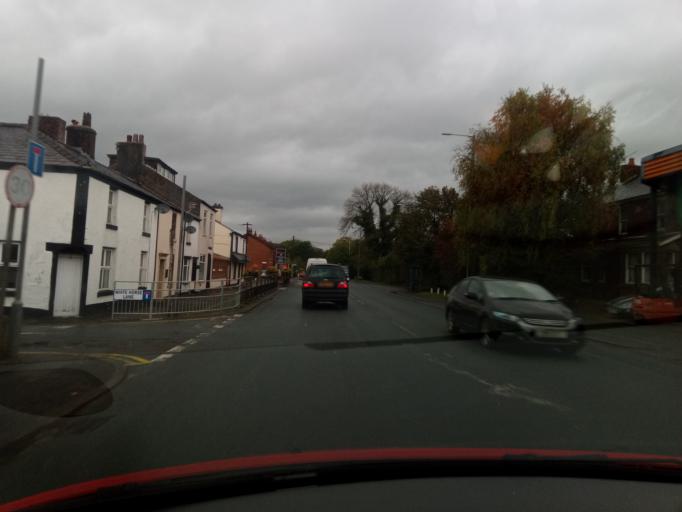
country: GB
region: England
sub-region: Lancashire
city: Catterall
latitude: 53.8377
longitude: -2.7395
